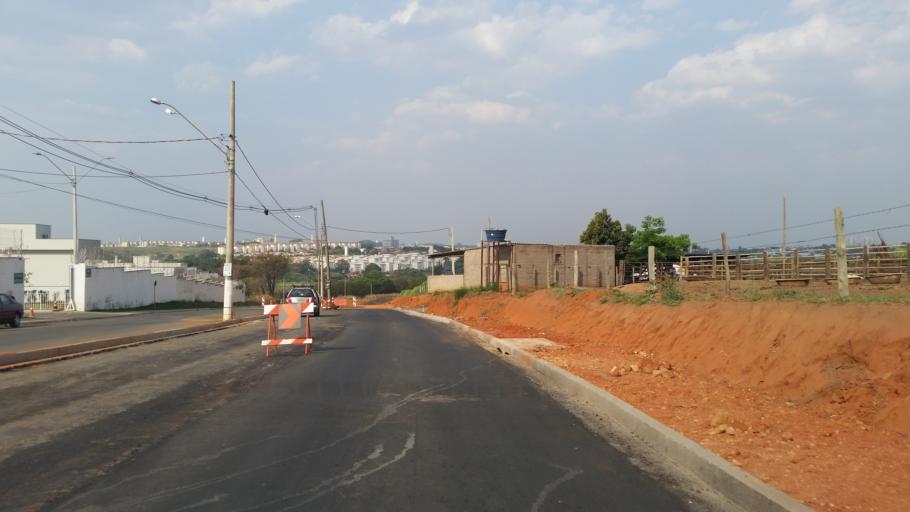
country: BR
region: Sao Paulo
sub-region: Hortolandia
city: Hortolandia
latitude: -22.8845
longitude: -47.1896
